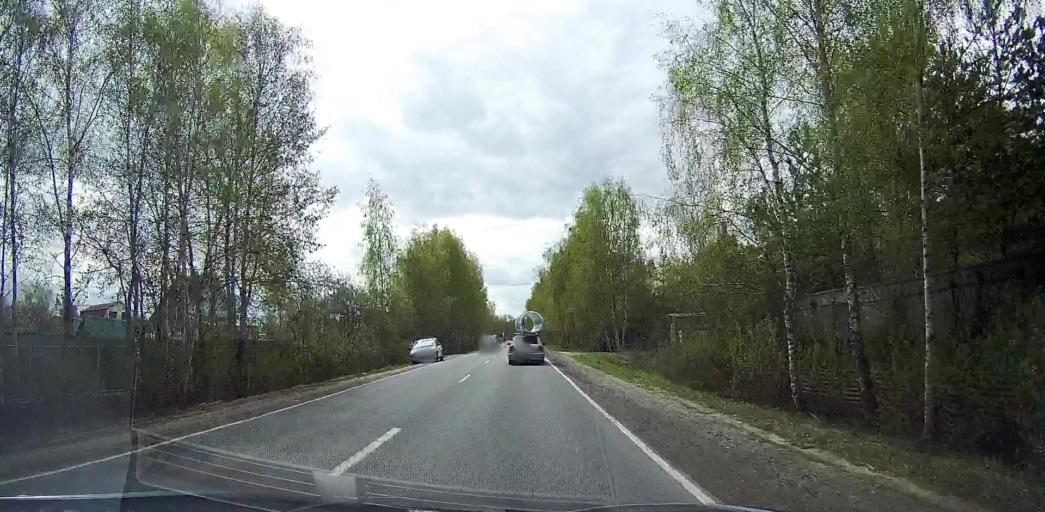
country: RU
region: Moskovskaya
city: Beloozerskiy
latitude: 55.4784
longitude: 38.4219
